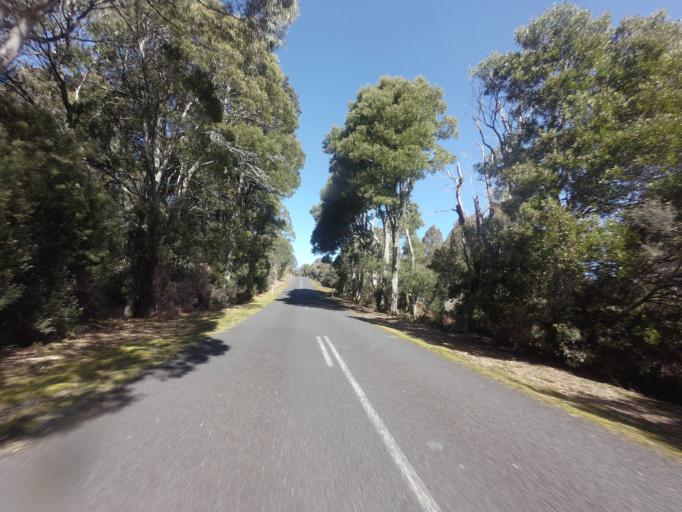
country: AU
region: Tasmania
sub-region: Derwent Valley
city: New Norfolk
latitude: -42.7600
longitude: 146.5309
